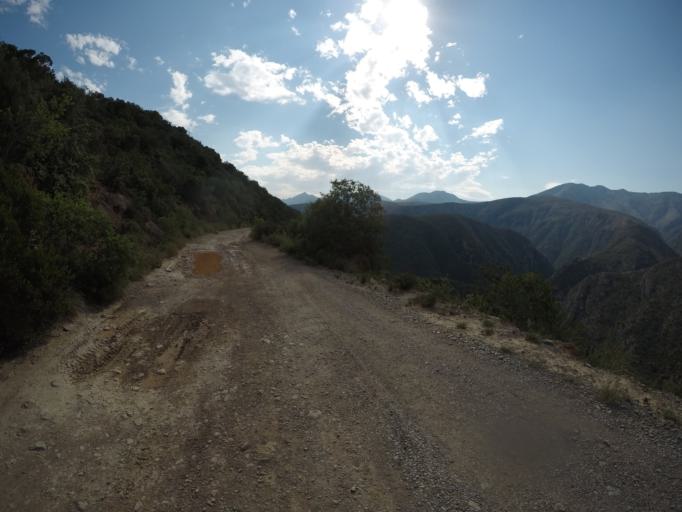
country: ZA
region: Eastern Cape
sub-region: Cacadu District Municipality
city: Kareedouw
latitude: -33.6486
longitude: 24.3480
